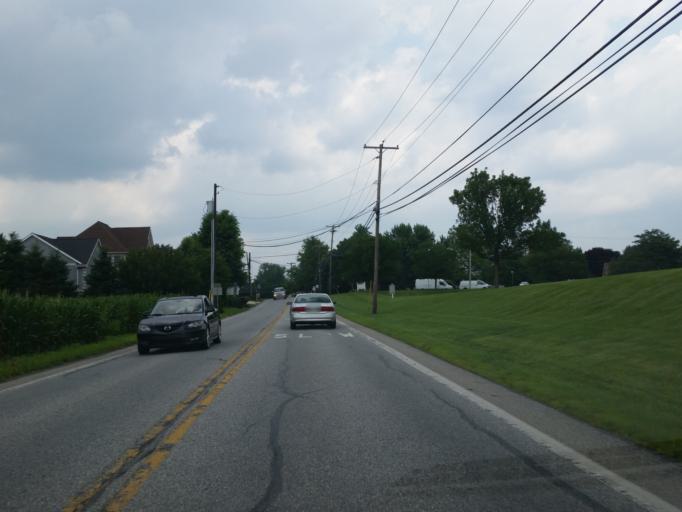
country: US
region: Pennsylvania
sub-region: Lebanon County
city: Campbelltown
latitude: 40.2964
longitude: -76.5765
